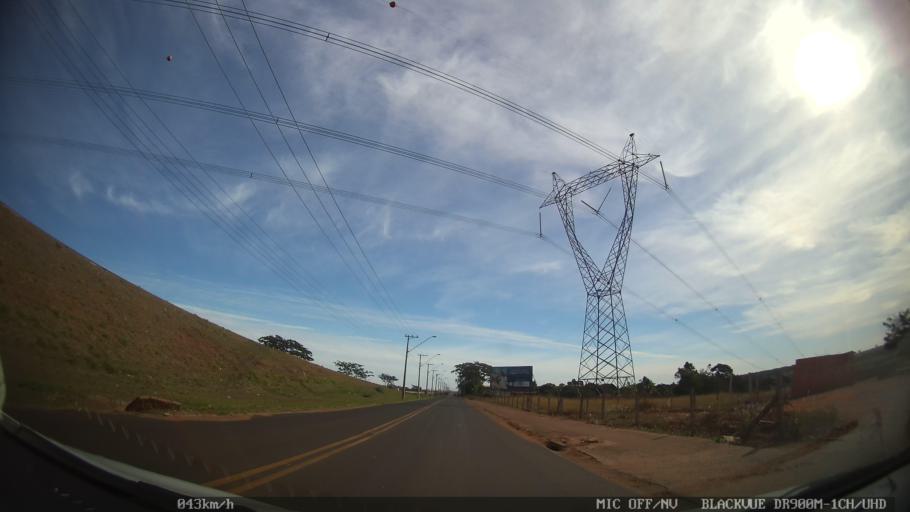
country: BR
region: Sao Paulo
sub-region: Guapiacu
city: Guapiacu
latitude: -20.7915
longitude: -49.3014
